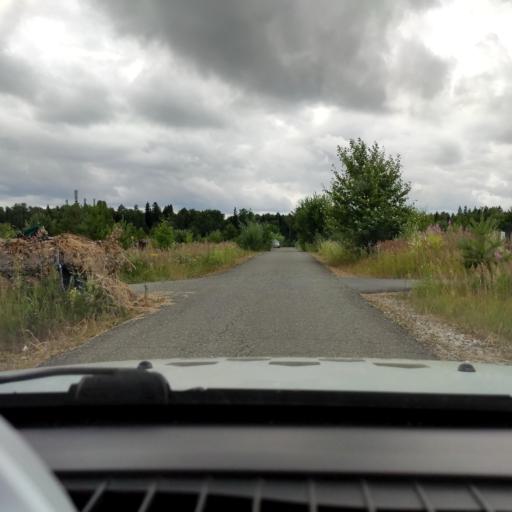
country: RU
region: Perm
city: Kondratovo
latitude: 58.0643
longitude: 56.1530
